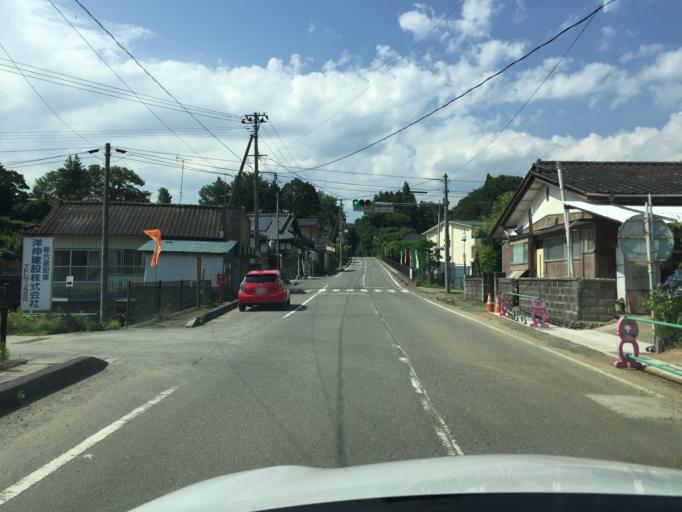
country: JP
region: Ibaraki
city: Kitaibaraki
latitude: 36.9623
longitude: 140.7037
